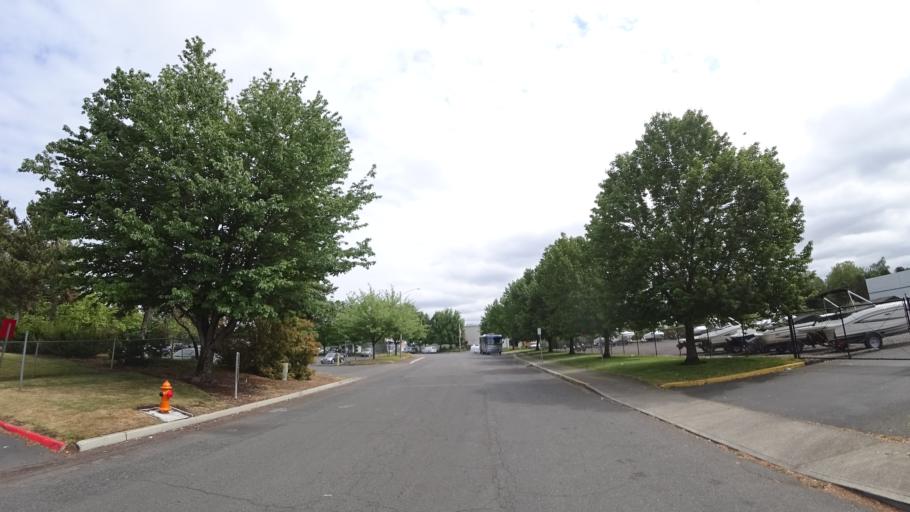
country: US
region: Washington
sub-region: Clark County
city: Vancouver
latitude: 45.6184
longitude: -122.6937
